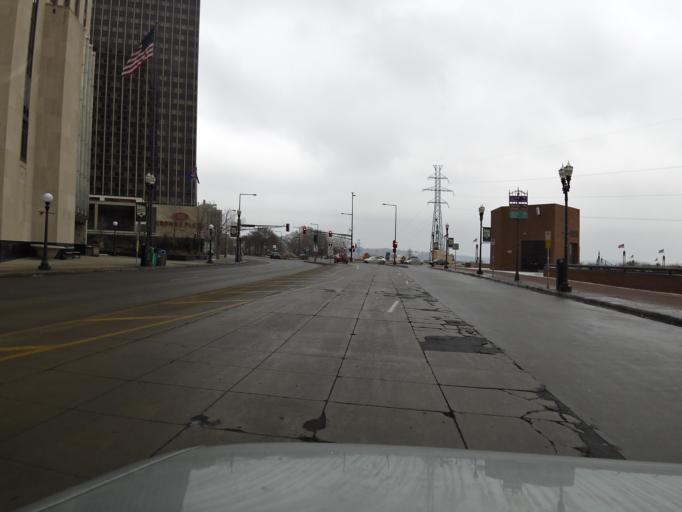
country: US
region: Minnesota
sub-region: Ramsey County
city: Saint Paul
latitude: 44.9438
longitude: -93.0940
